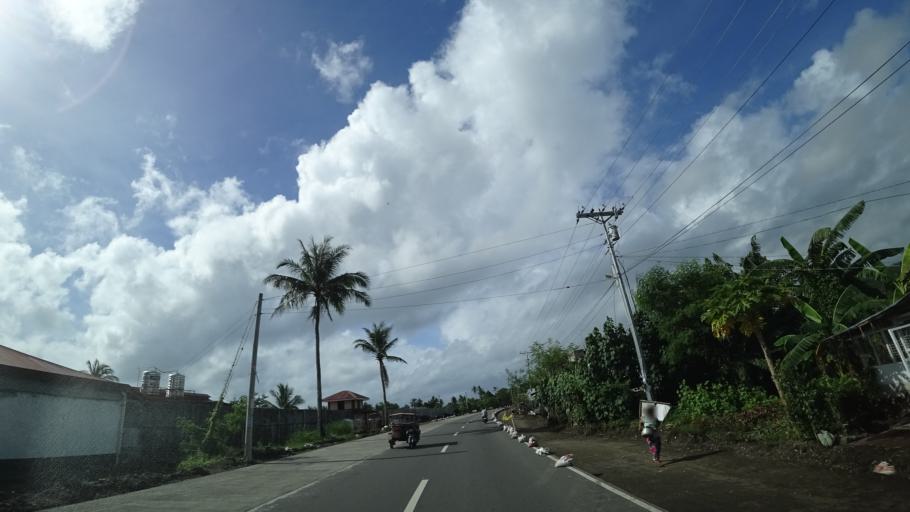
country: PH
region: Eastern Visayas
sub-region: Province of Leyte
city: San Roque
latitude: 11.0296
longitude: 125.0360
